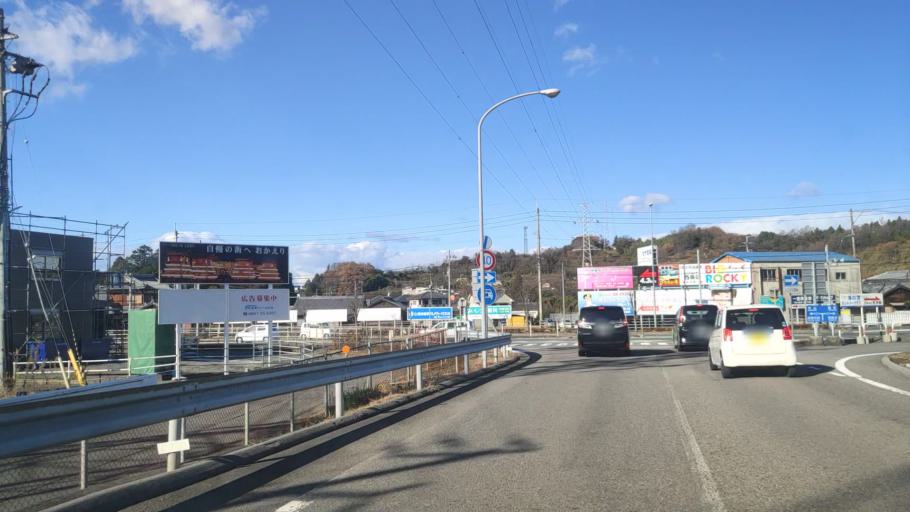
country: JP
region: Ehime
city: Saijo
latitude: 33.9192
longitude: 133.2402
